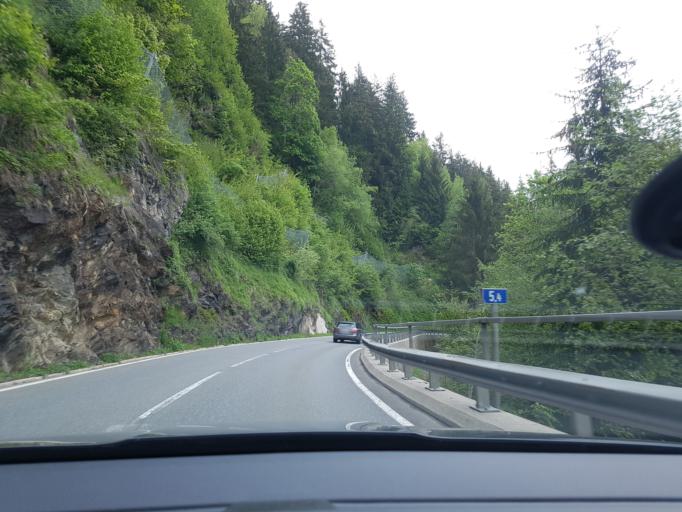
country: AT
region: Salzburg
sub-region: Politischer Bezirk Zell am See
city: Hollersbach im Pinzgau
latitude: 47.2932
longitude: 12.4454
